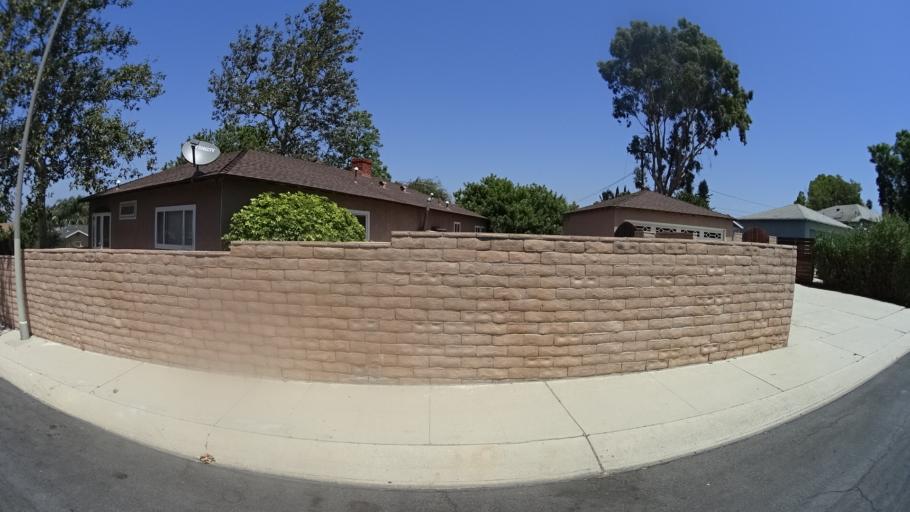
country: US
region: California
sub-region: Los Angeles County
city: Ladera Heights
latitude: 34.0169
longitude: -118.3630
